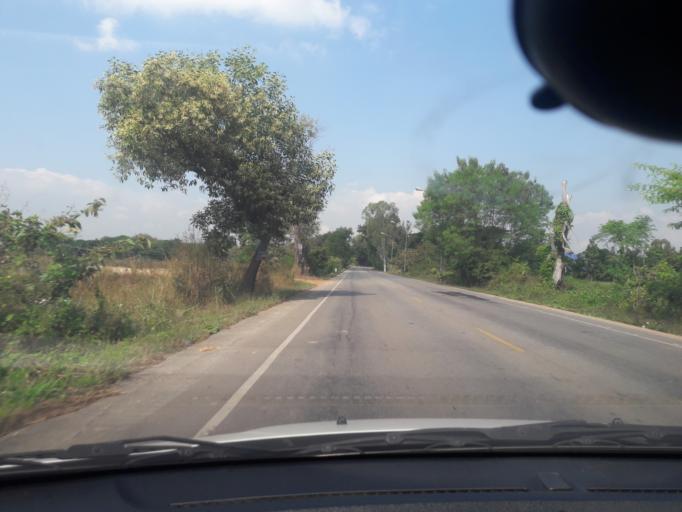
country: TH
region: Lampang
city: Mae Tha
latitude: 18.2086
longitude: 99.4966
